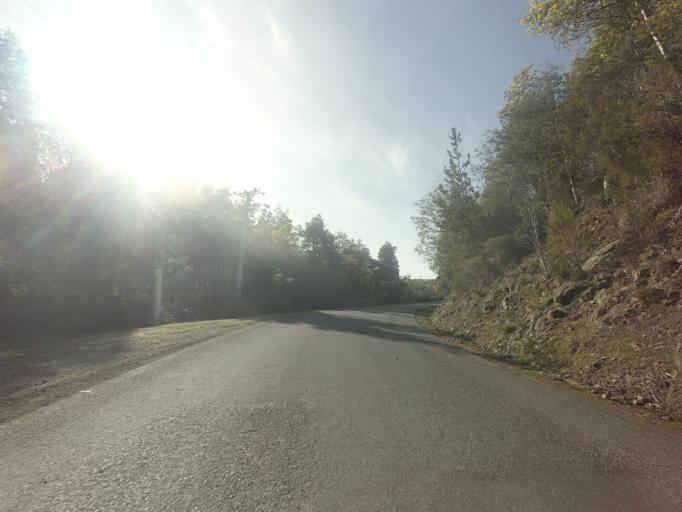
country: AU
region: Tasmania
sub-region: Huon Valley
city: Cygnet
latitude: -43.1762
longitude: 147.1505
